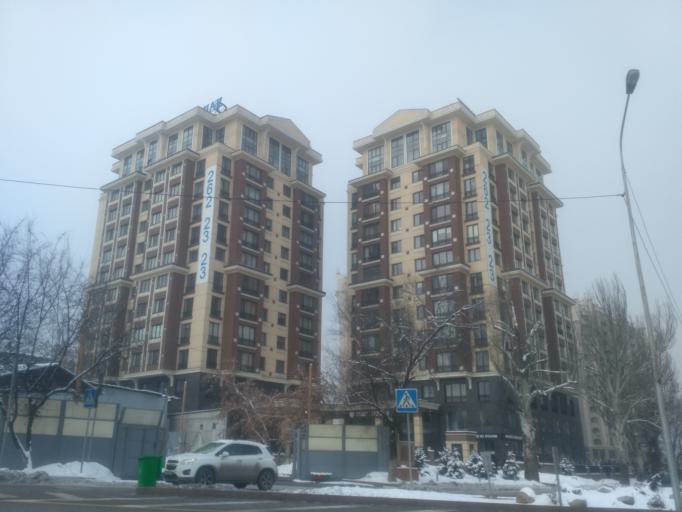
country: KZ
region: Almaty Qalasy
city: Almaty
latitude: 43.2064
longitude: 76.9136
